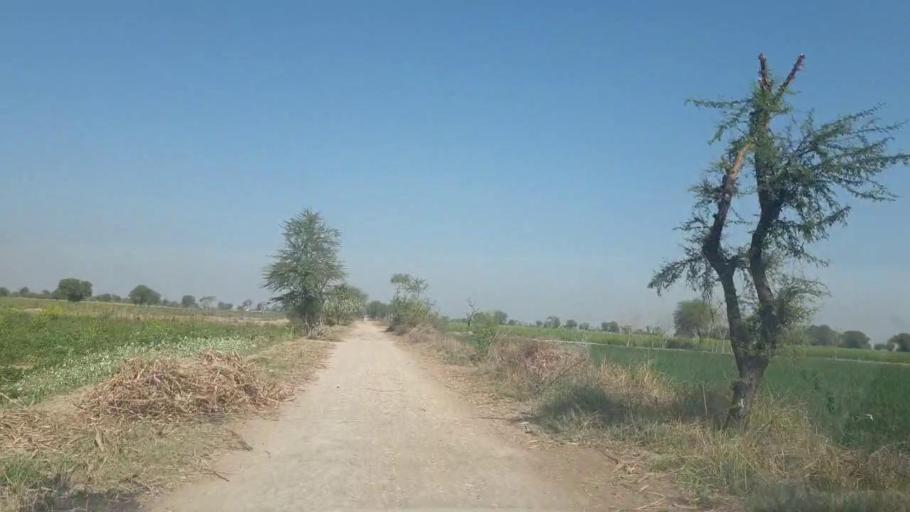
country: PK
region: Sindh
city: Mirpur Khas
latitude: 25.5475
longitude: 69.1965
